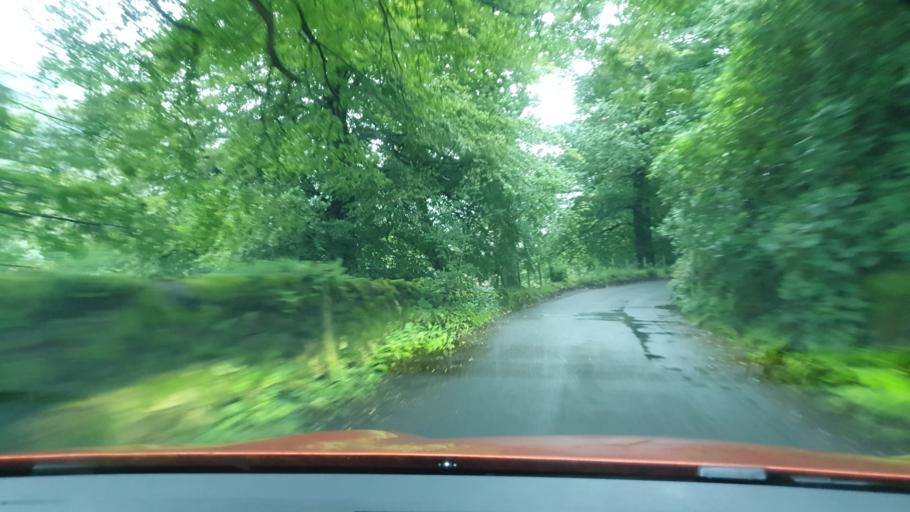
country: GB
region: England
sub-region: Cumbria
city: Seascale
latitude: 54.4306
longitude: -3.3179
